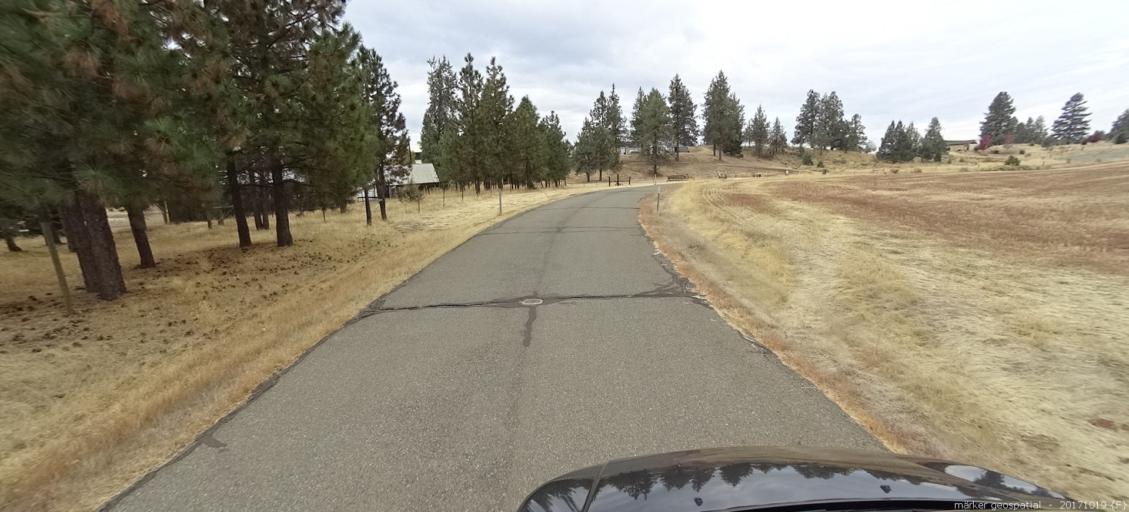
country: US
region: California
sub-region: Shasta County
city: Burney
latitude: 41.0580
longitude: -121.3721
